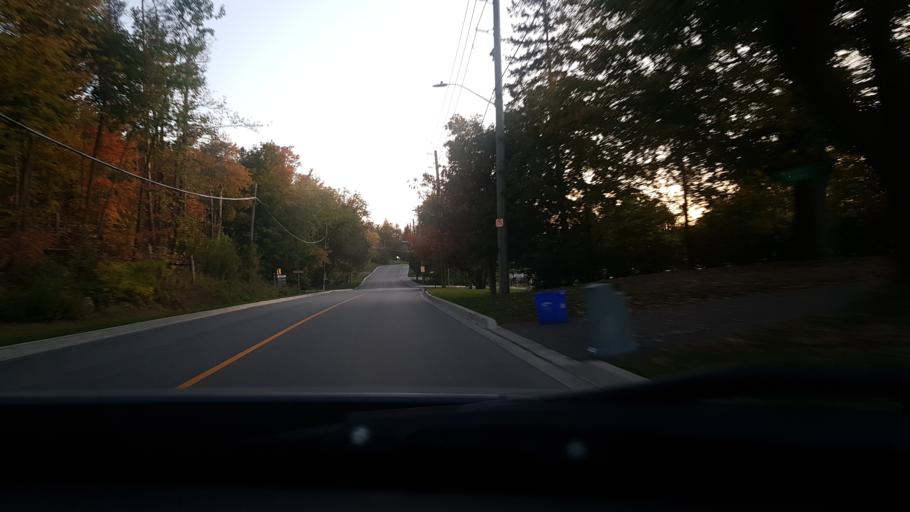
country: CA
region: Ontario
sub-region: Halton
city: Milton
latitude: 43.4907
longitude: -79.9794
